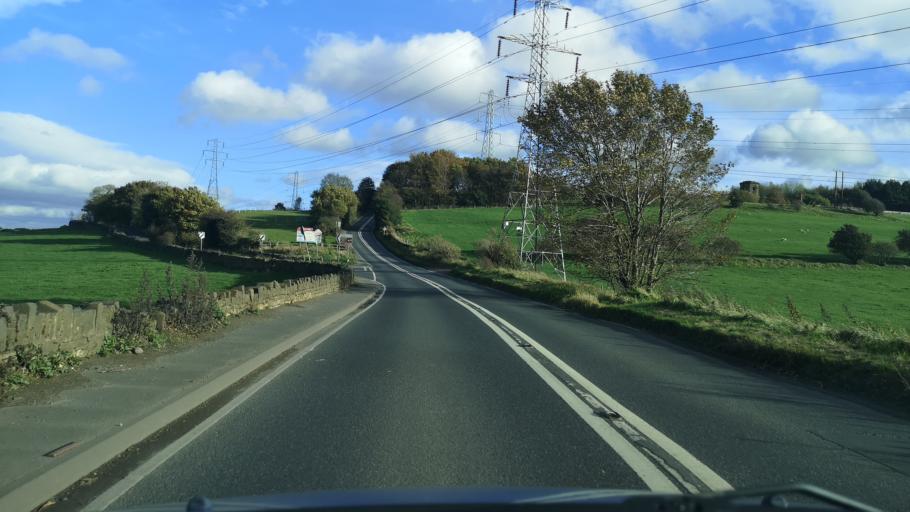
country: GB
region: England
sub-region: Kirklees
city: Mirfield
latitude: 53.6512
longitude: -1.6896
